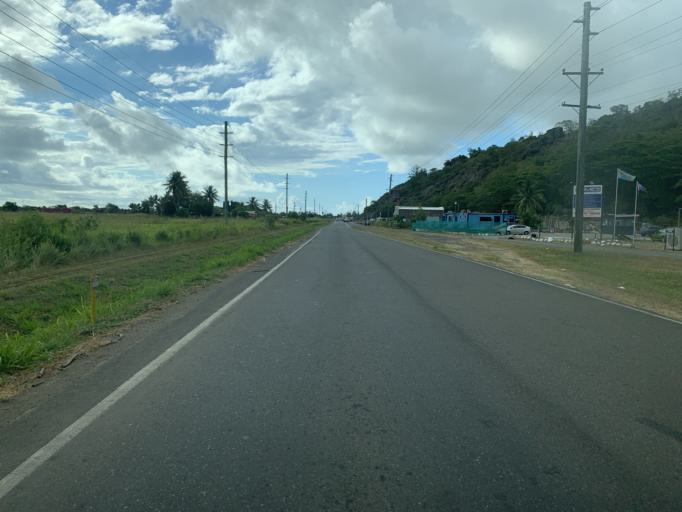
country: FJ
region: Western
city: Lautoka
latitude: -17.7081
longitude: 177.4420
